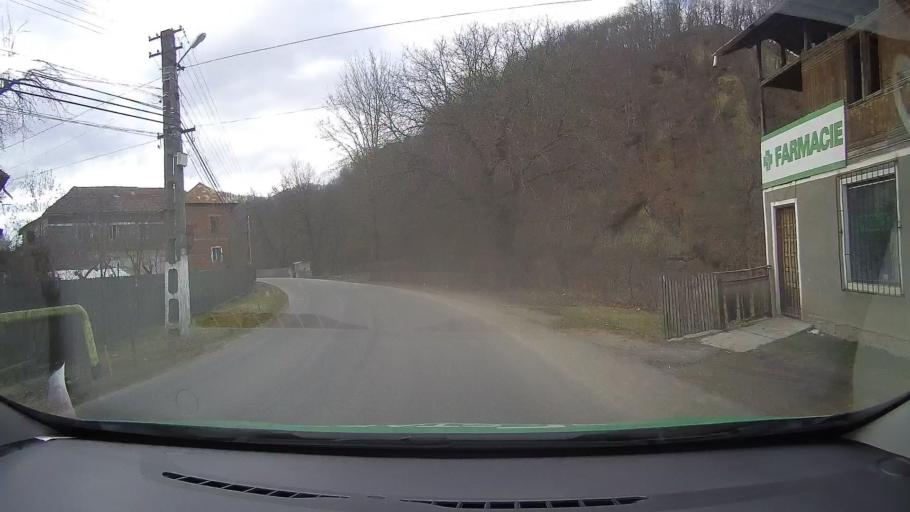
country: RO
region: Dambovita
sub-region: Comuna Visinesti
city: Visinesti
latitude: 45.1099
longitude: 25.5515
